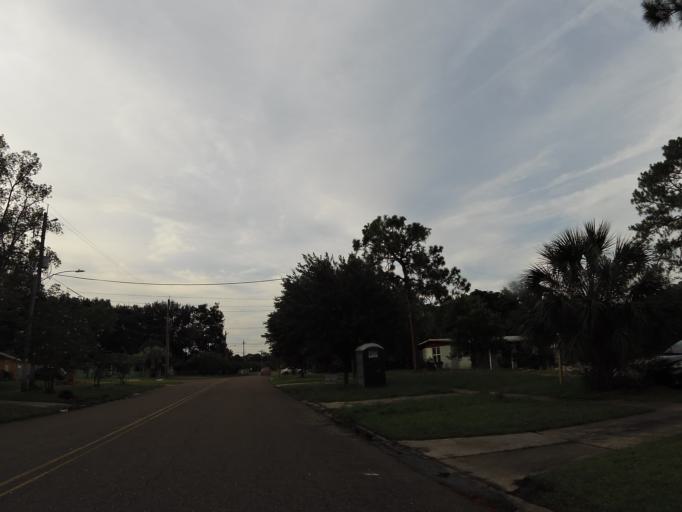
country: US
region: Florida
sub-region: Duval County
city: Jacksonville
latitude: 30.4001
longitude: -81.7197
